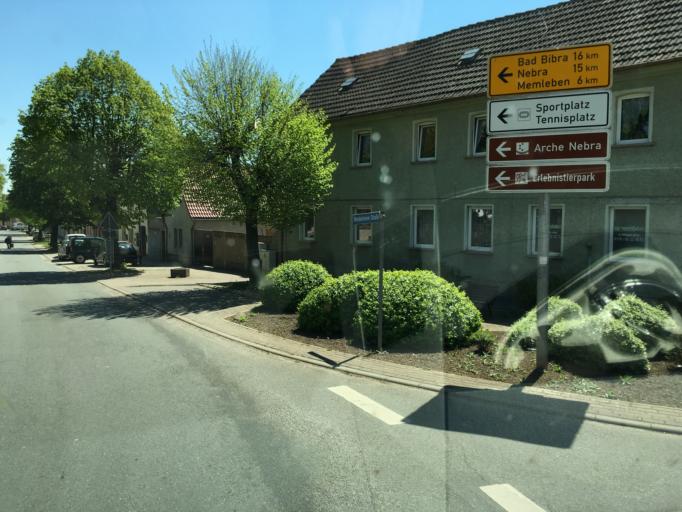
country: DE
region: Thuringia
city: Rossleben
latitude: 51.2966
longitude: 11.4329
